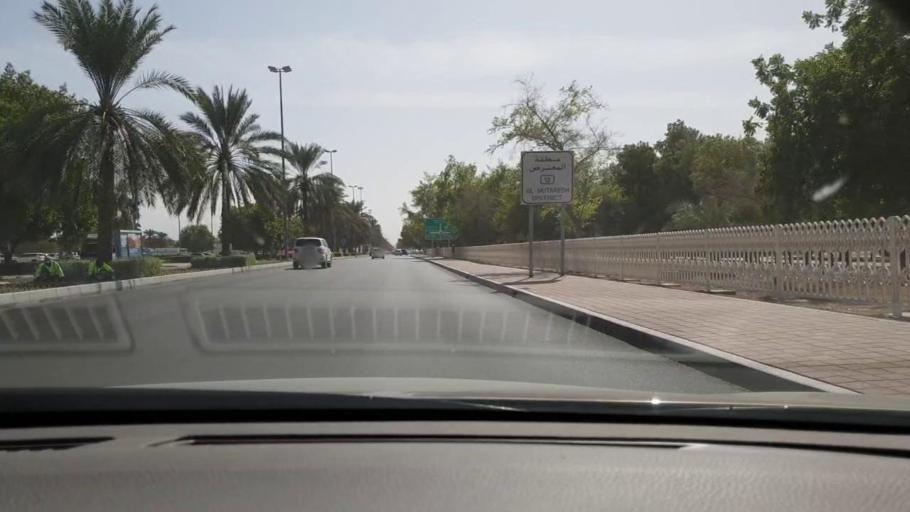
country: AE
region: Abu Dhabi
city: Al Ain
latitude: 24.2343
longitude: 55.7385
